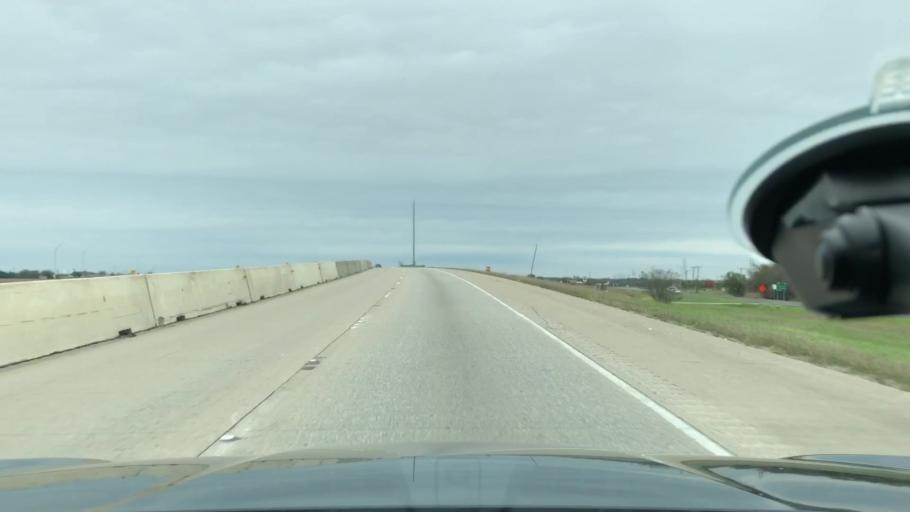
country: US
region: Texas
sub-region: Ellis County
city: Waxahachie
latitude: 32.3610
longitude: -96.8551
